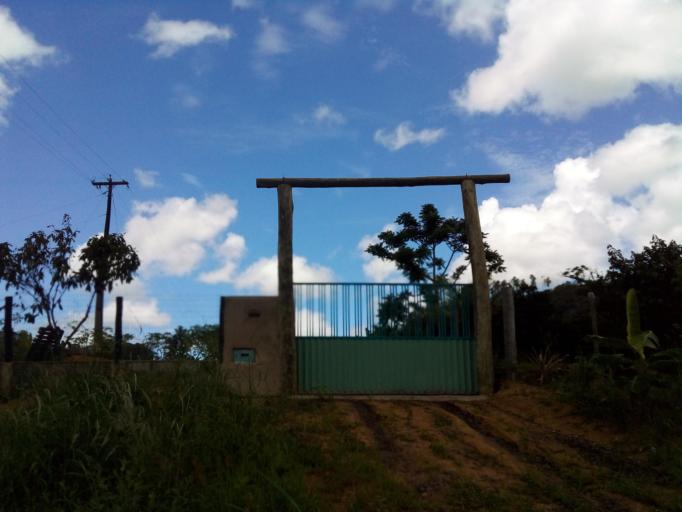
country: BR
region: Espirito Santo
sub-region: Ibiracu
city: Ibiracu
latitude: -19.8641
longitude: -40.3615
